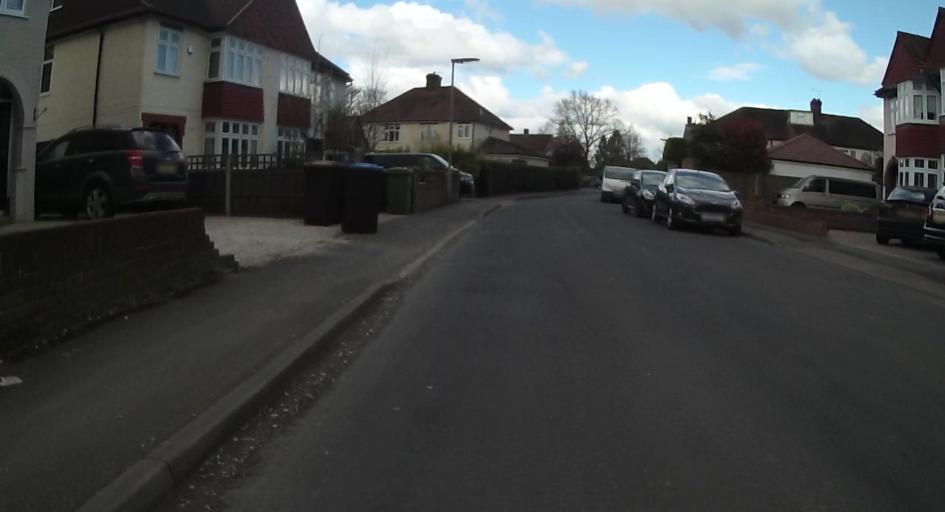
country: GB
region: England
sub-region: Surrey
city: Addlestone
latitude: 51.3684
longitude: -0.4994
